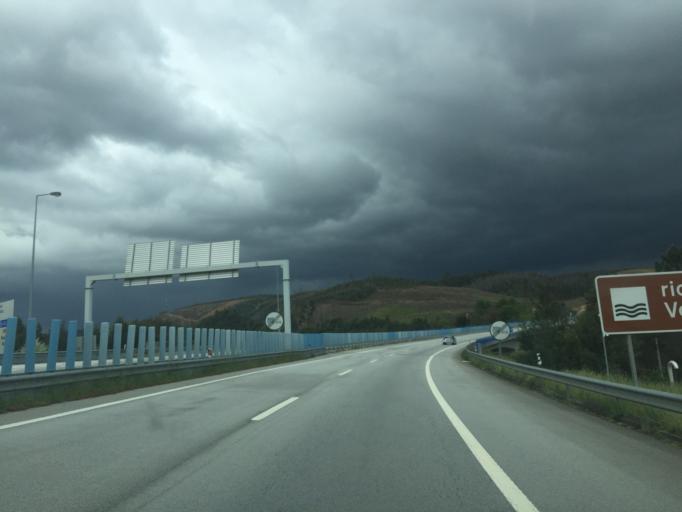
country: PT
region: Aveiro
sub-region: Albergaria-A-Velha
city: Albergaria-a-Velha
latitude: 40.6784
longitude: -8.4407
